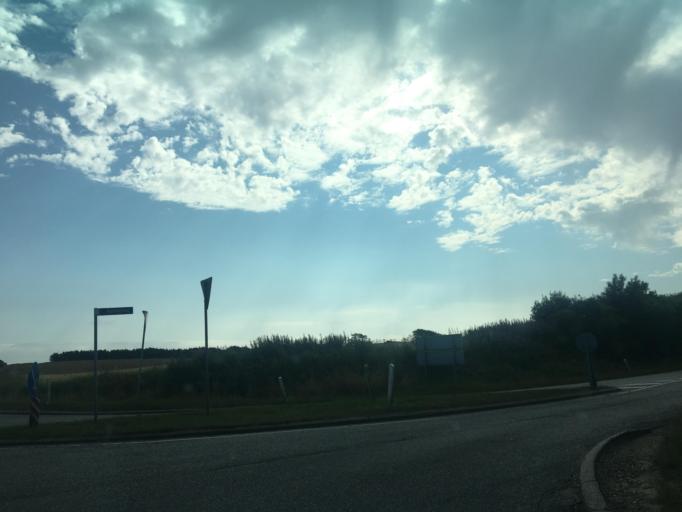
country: DK
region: North Denmark
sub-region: Thisted Kommune
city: Hurup
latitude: 56.7586
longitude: 8.4511
